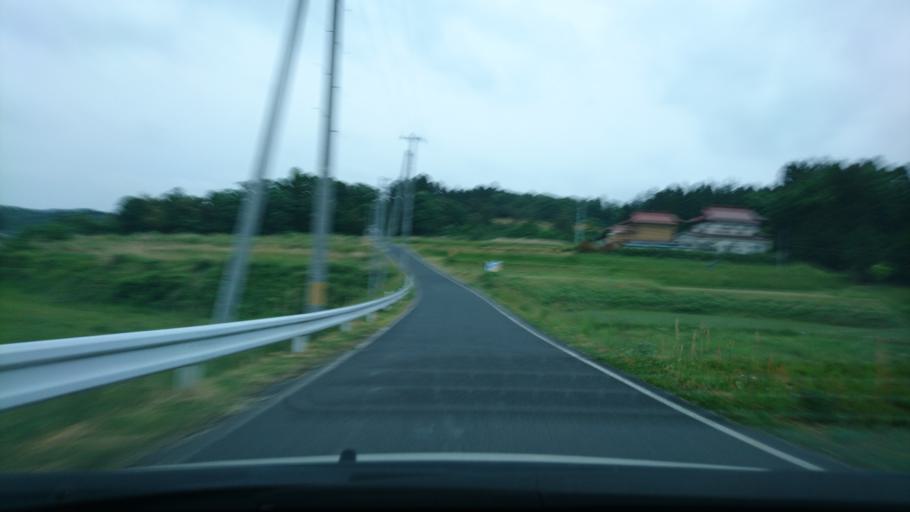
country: JP
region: Iwate
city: Ichinoseki
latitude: 38.9178
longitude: 141.1740
